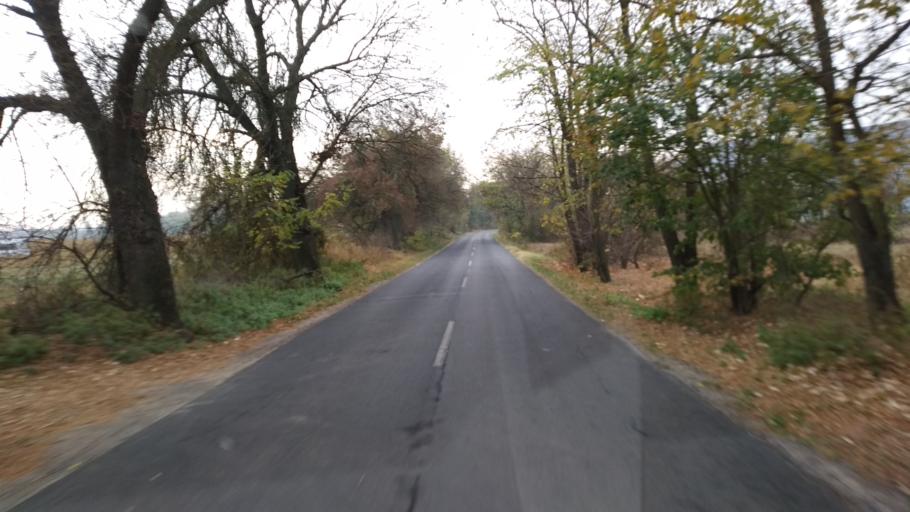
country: HU
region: Pest
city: Tahitotfalu
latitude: 47.7629
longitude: 19.0858
